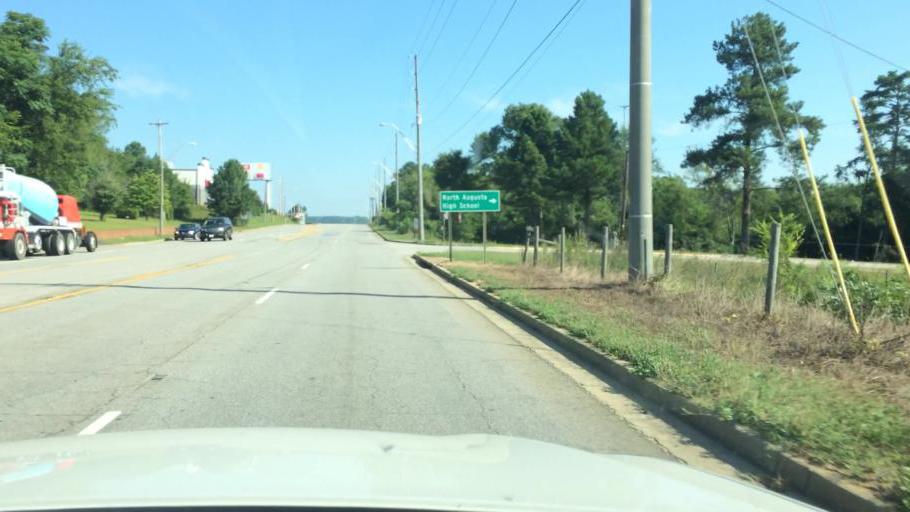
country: US
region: South Carolina
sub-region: Aiken County
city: North Augusta
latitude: 33.5338
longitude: -81.9868
